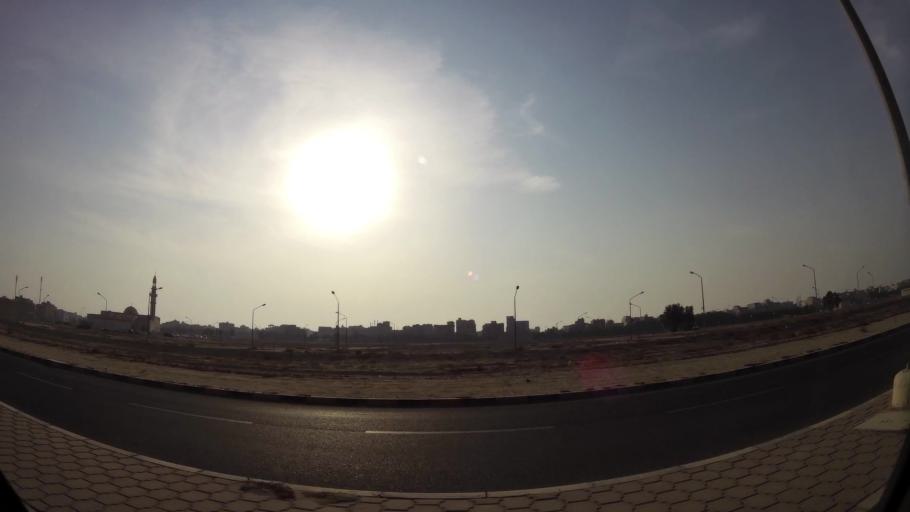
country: KW
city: Al Funaytis
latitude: 29.2388
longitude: 48.0873
